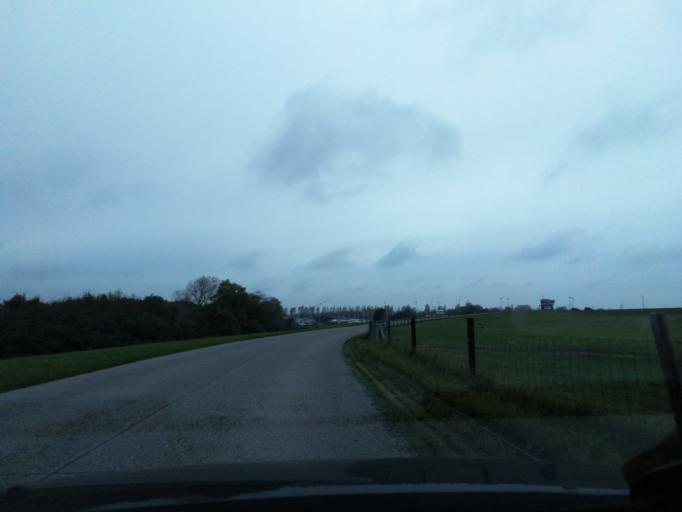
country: DE
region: Lower Saxony
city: Fedderwarden
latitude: 53.6389
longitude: 8.0848
